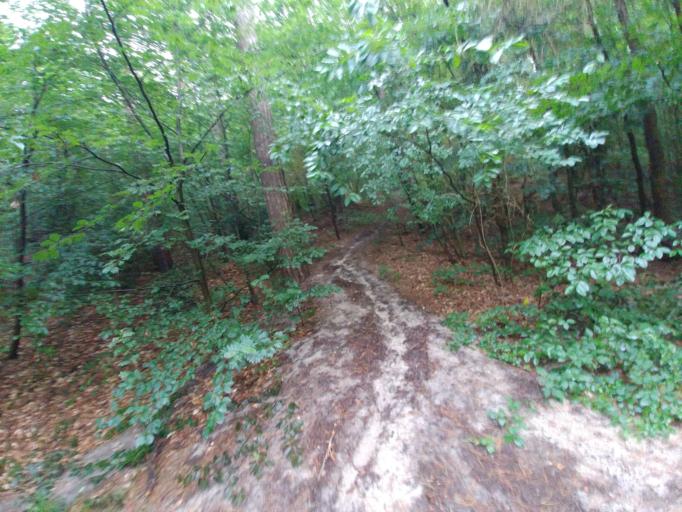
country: NL
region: North Holland
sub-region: Gemeente Alkmaar
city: Alkmaar
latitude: 52.6854
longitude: 4.6948
